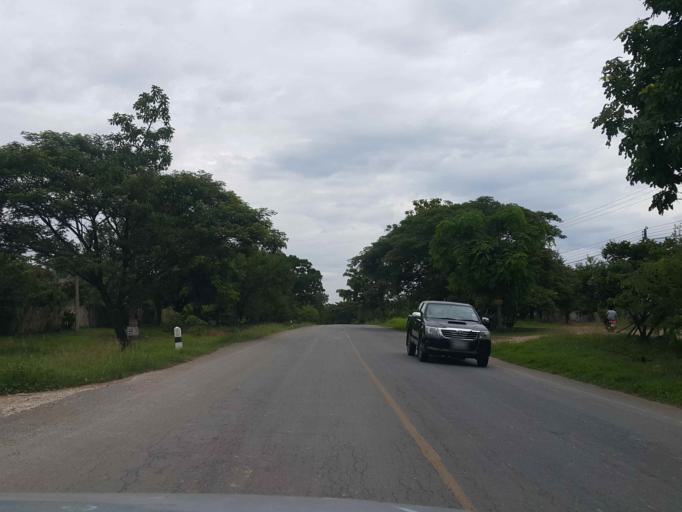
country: TH
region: Lampang
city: Thoen
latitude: 17.5705
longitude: 99.3292
